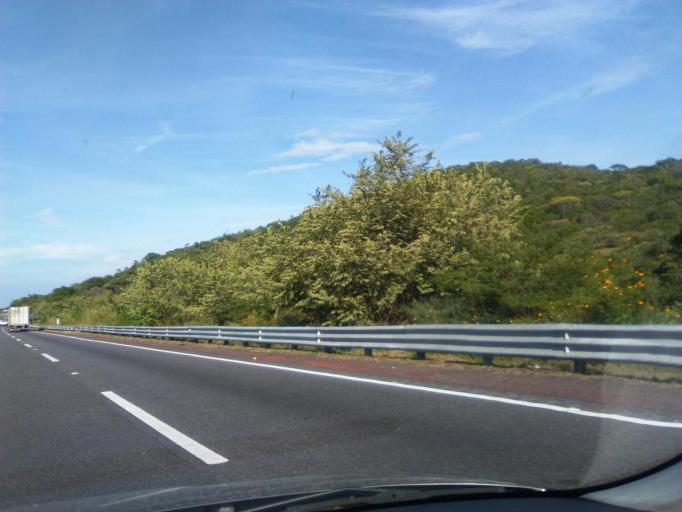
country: MX
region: Guerrero
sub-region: Huitzuco de los Figueroa
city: Ciudad de Huitzuco
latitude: 18.2881
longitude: -99.2083
